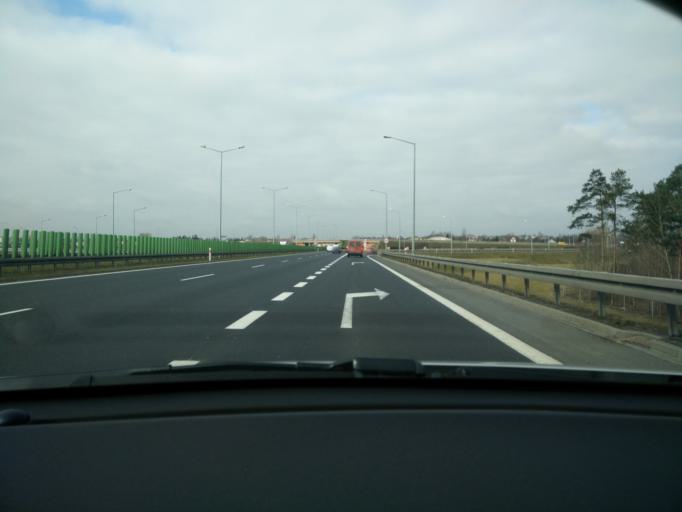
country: PL
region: Greater Poland Voivodeship
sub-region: Powiat poznanski
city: Lubon
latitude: 52.3536
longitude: 16.9084
